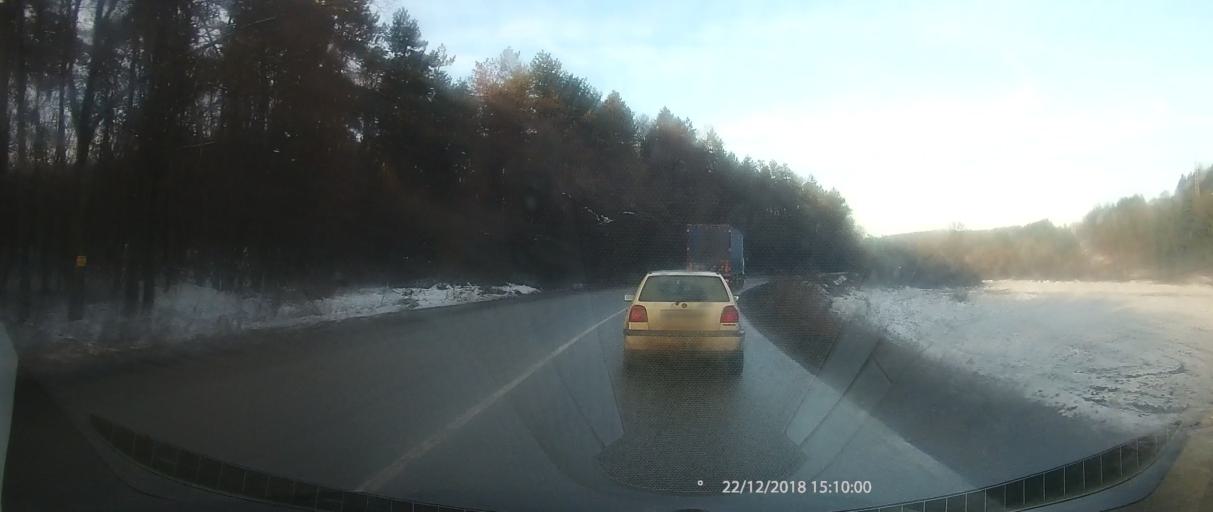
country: BG
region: Ruse
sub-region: Obshtina Borovo
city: Borovo
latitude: 43.5104
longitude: 25.7964
